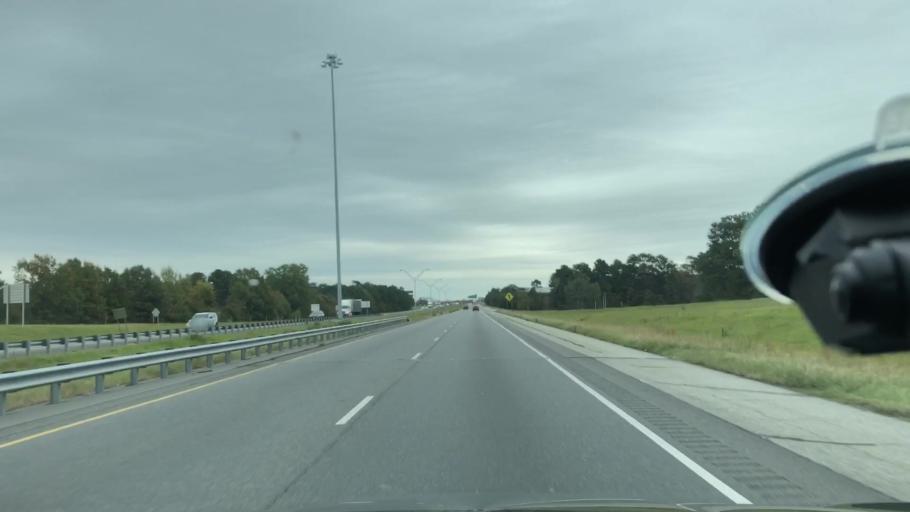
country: US
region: Arkansas
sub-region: Miller County
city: Texarkana
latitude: 33.4759
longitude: -94.0064
